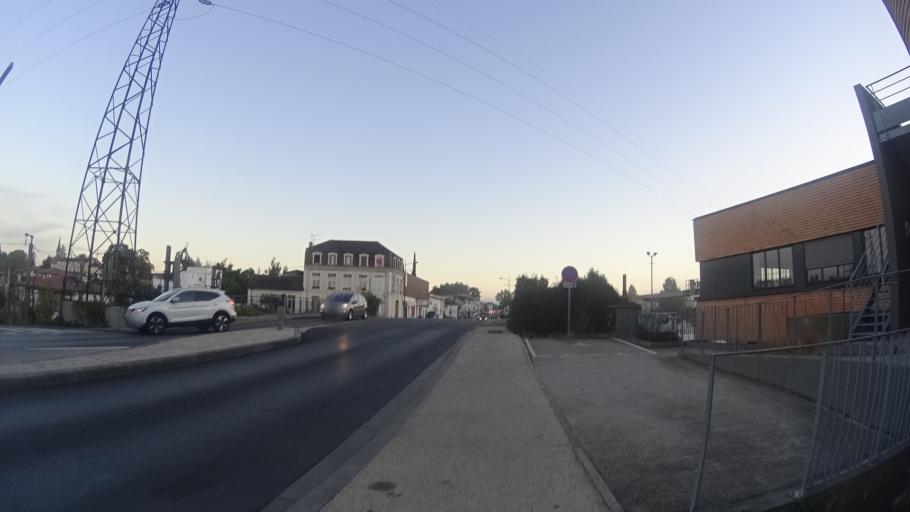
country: FR
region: Aquitaine
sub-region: Departement des Landes
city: Saint-Paul-les-Dax
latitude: 43.7205
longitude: -1.0522
